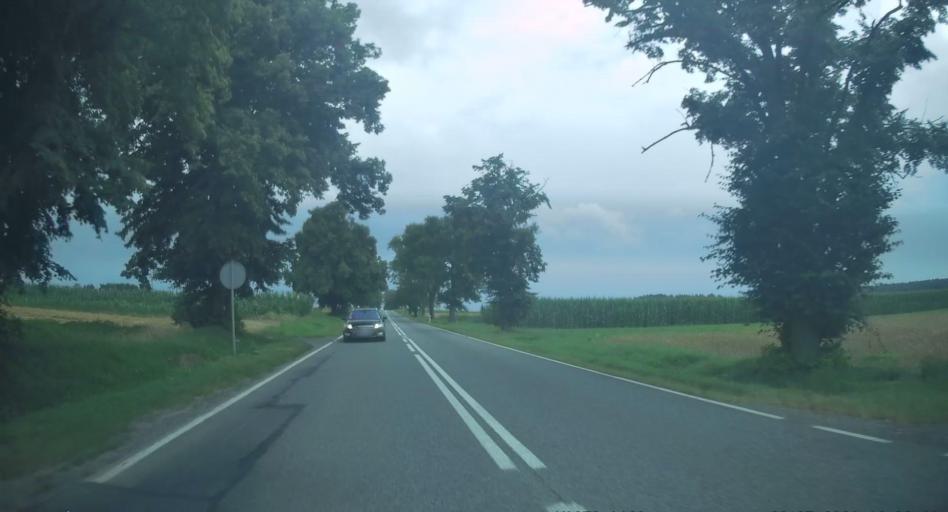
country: PL
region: Lodz Voivodeship
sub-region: Powiat skierniewicki
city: Gluchow
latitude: 51.7780
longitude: 20.1003
